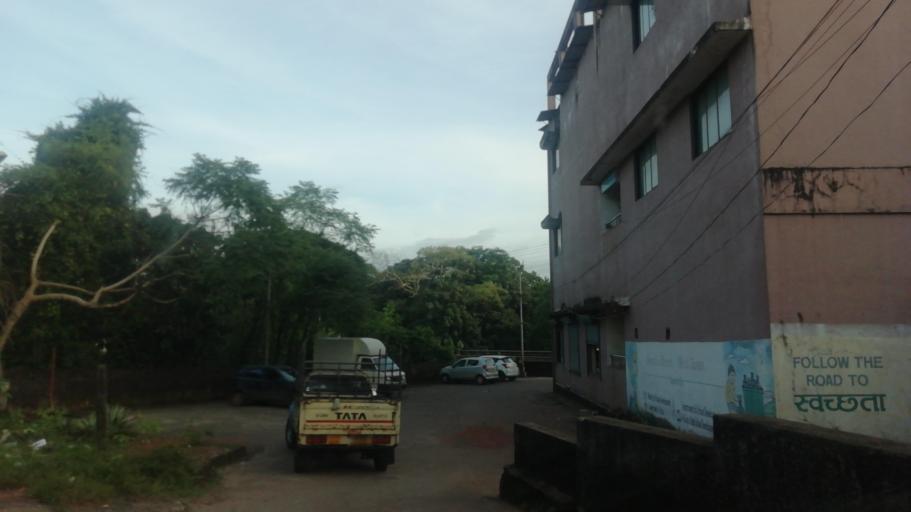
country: IN
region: Goa
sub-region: North Goa
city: Valpoy
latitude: 15.5298
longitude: 74.1351
